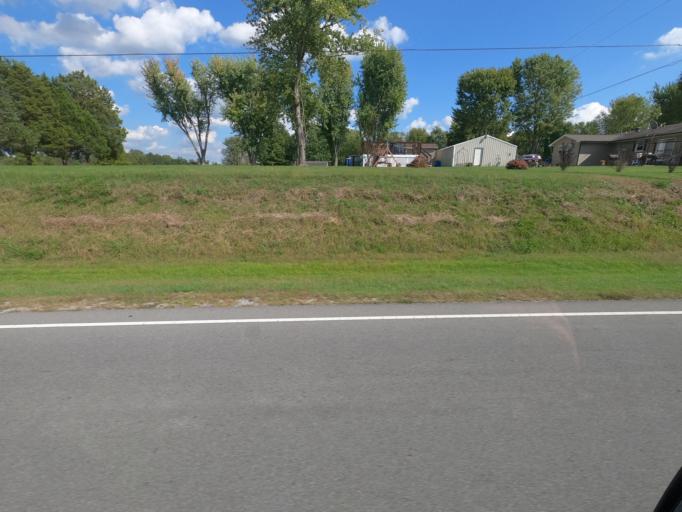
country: US
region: Illinois
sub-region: Massac County
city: Metropolis
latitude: 37.1701
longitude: -88.6766
